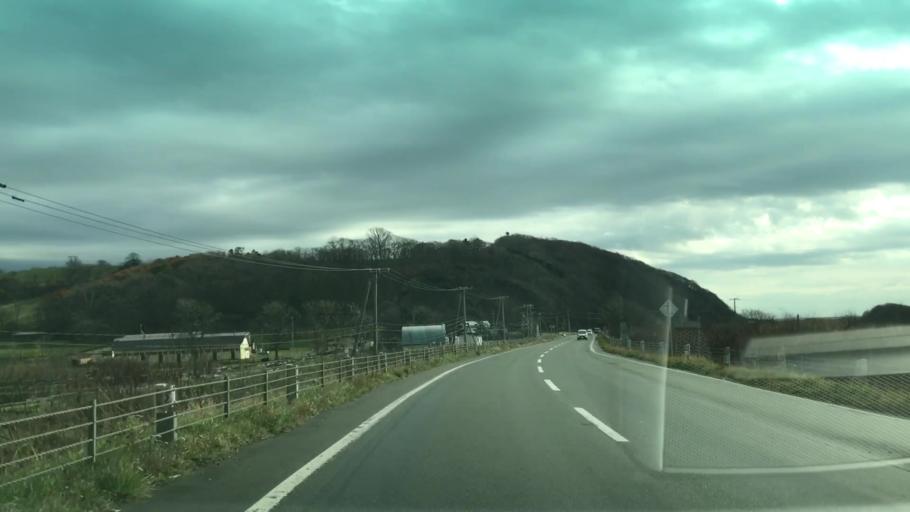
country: JP
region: Hokkaido
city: Shizunai-furukawacho
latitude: 42.1421
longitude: 142.8510
